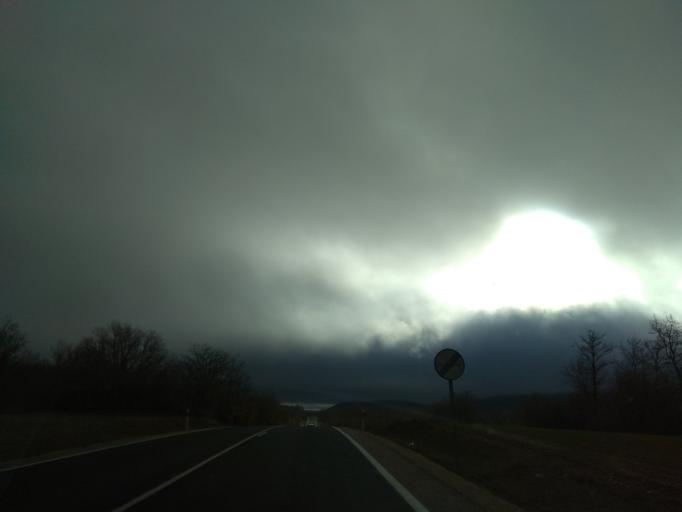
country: ES
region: Castille and Leon
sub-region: Provincia de Burgos
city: Tubilla del Agua
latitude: 42.6330
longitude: -3.8670
